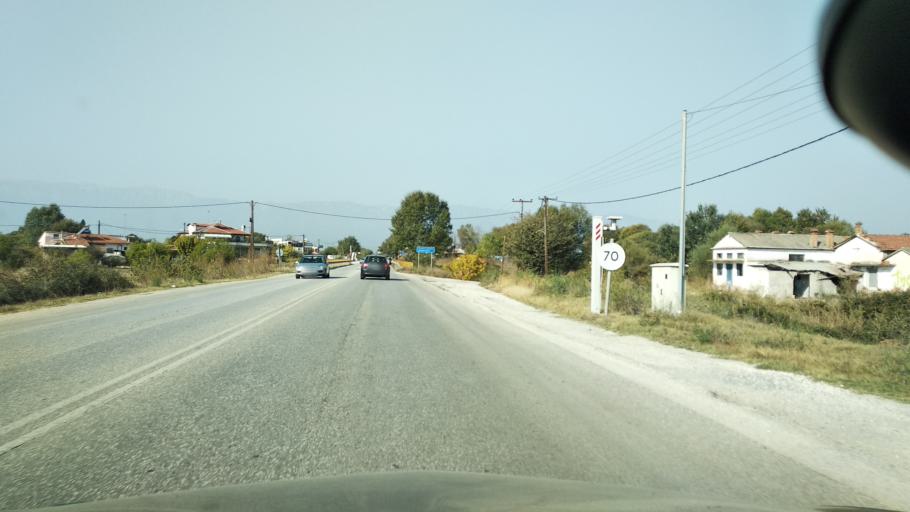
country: GR
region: Thessaly
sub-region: Trikala
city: Trikala
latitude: 39.5705
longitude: 21.7573
